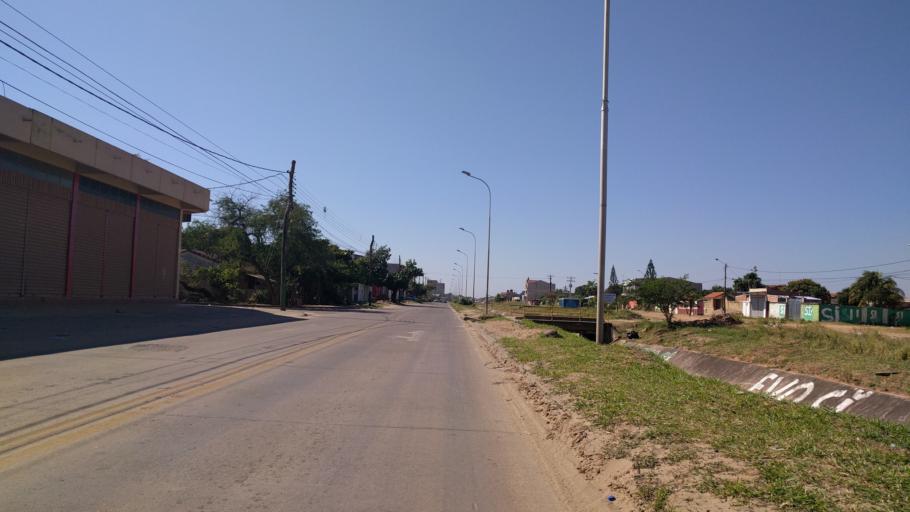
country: BO
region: Santa Cruz
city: Santa Cruz de la Sierra
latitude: -17.8434
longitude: -63.1870
